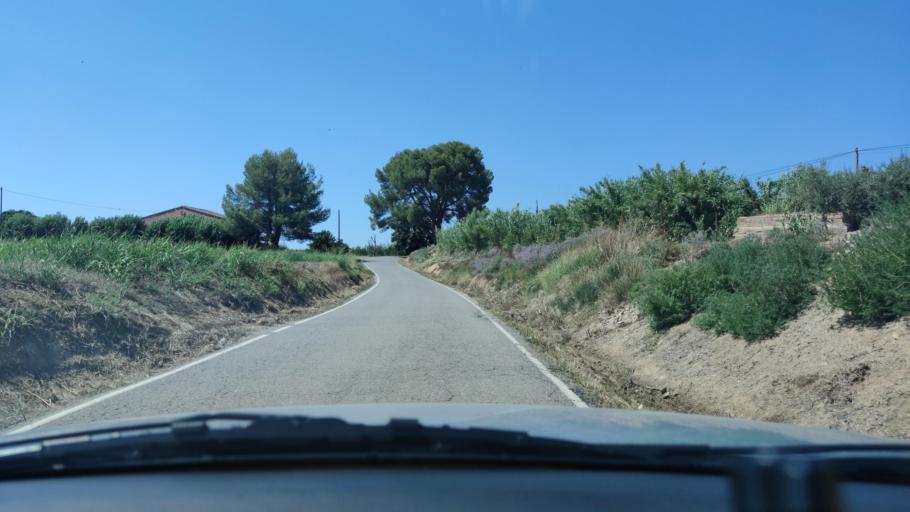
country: ES
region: Catalonia
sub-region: Provincia de Lleida
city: Torrefarrera
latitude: 41.6533
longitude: 0.6221
